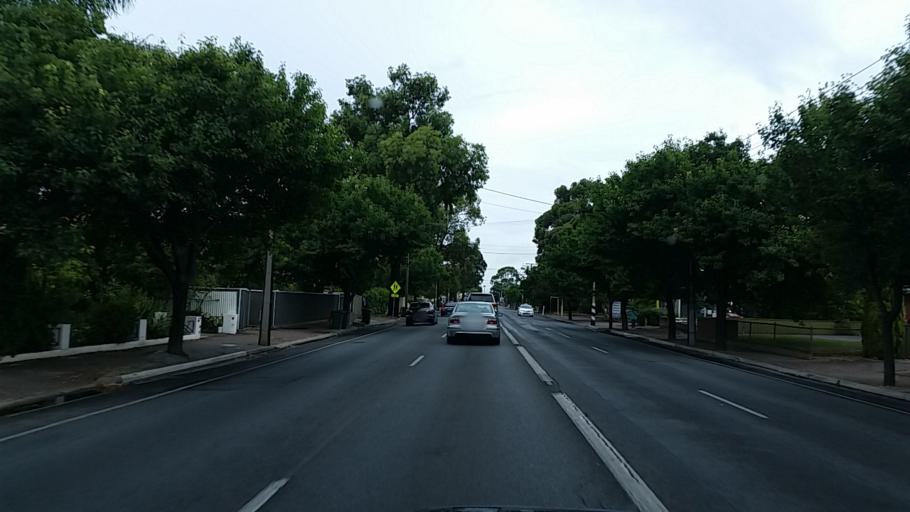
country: AU
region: South Australia
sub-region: Norwood Payneham St Peters
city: Royston Park
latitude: -34.9044
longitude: 138.6322
